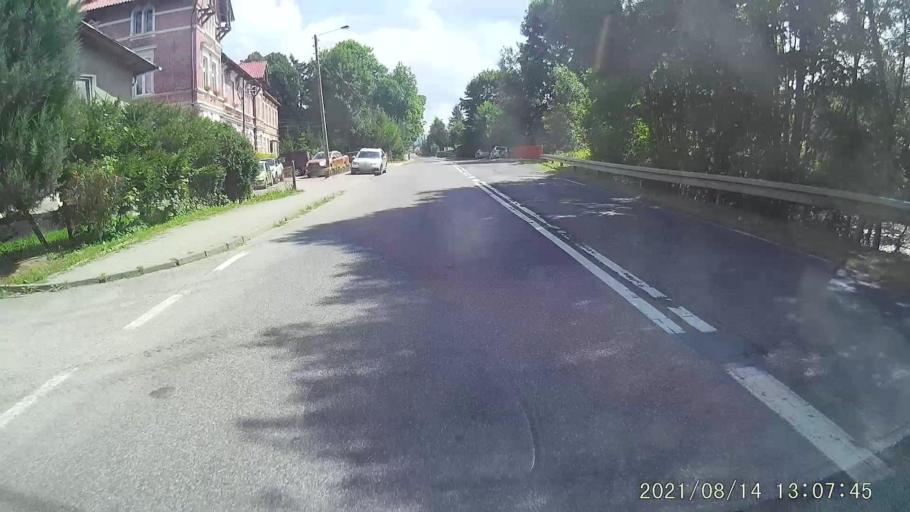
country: PL
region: Lower Silesian Voivodeship
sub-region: Powiat klodzki
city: Klodzko
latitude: 50.3685
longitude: 16.7045
